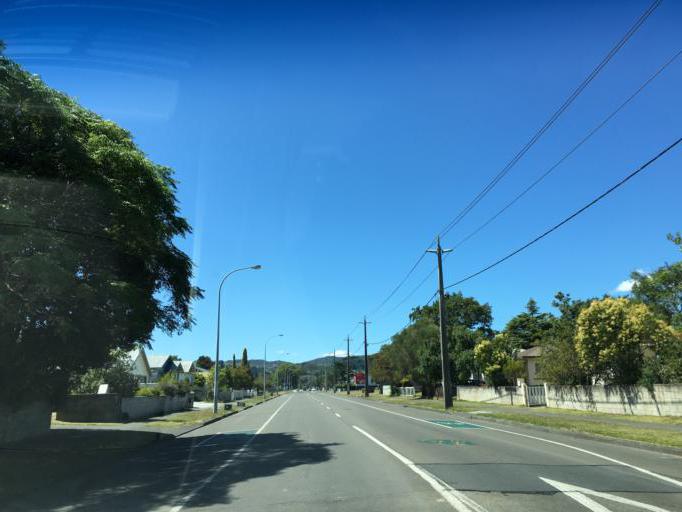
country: NZ
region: Gisborne
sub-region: Gisborne District
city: Gisborne
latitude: -38.6599
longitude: 178.0080
